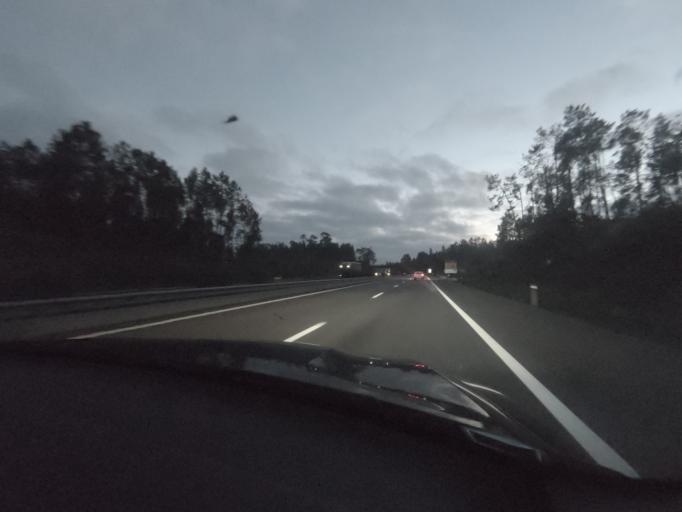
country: PT
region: Leiria
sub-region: Pombal
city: Pombal
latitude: 39.9213
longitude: -8.6827
